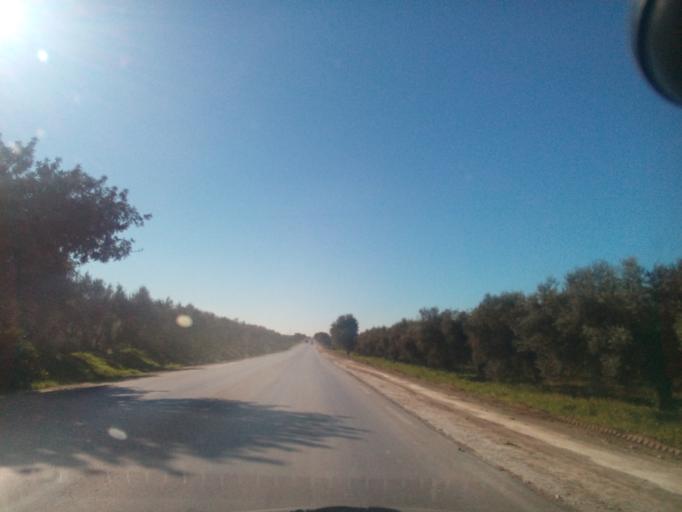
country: DZ
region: Relizane
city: Djidiouia
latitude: 35.9279
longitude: 0.8105
